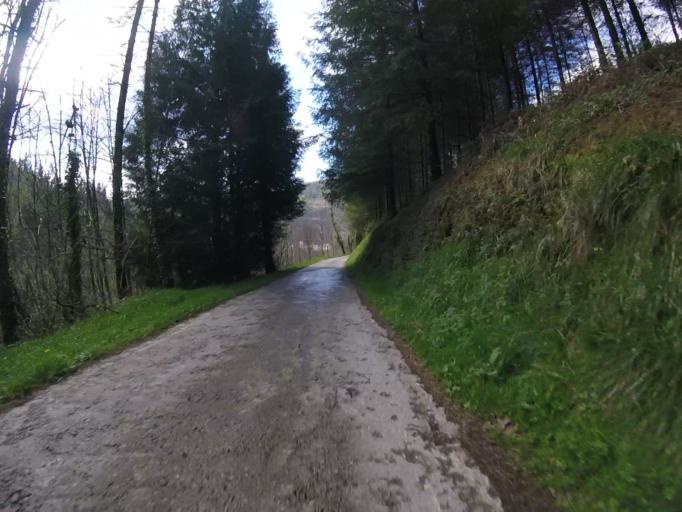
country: ES
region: Basque Country
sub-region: Provincia de Guipuzcoa
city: Albiztur
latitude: 43.1330
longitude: -2.1224
